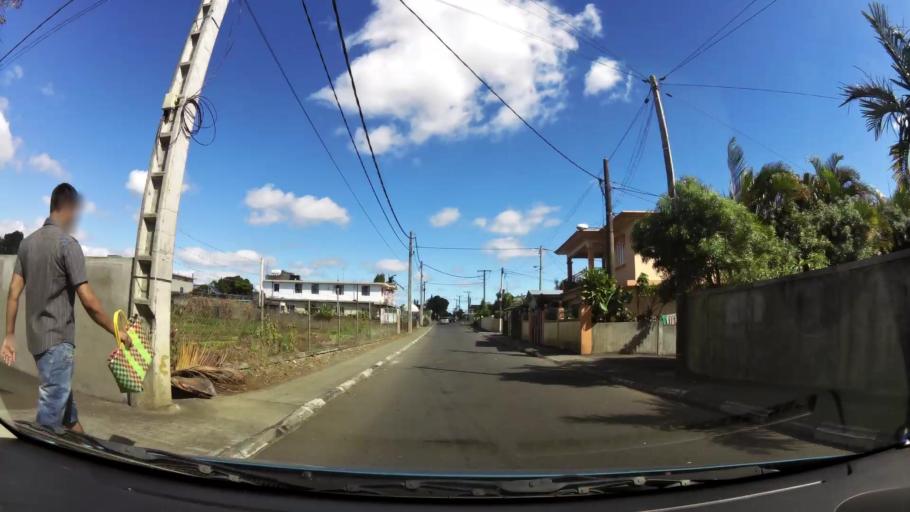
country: MU
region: Plaines Wilhems
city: Vacoas
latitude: -20.2871
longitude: 57.4783
